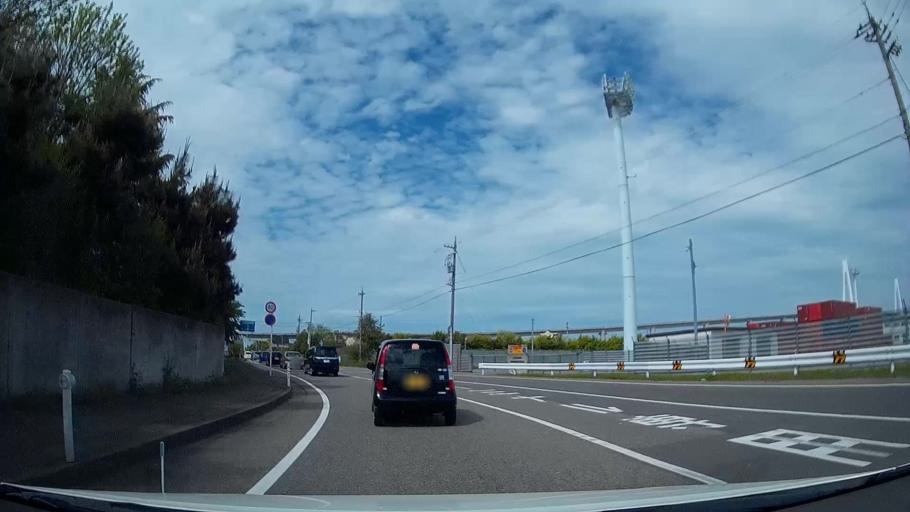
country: JP
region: Toyama
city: Nishishinminato
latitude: 36.7756
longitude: 137.1045
